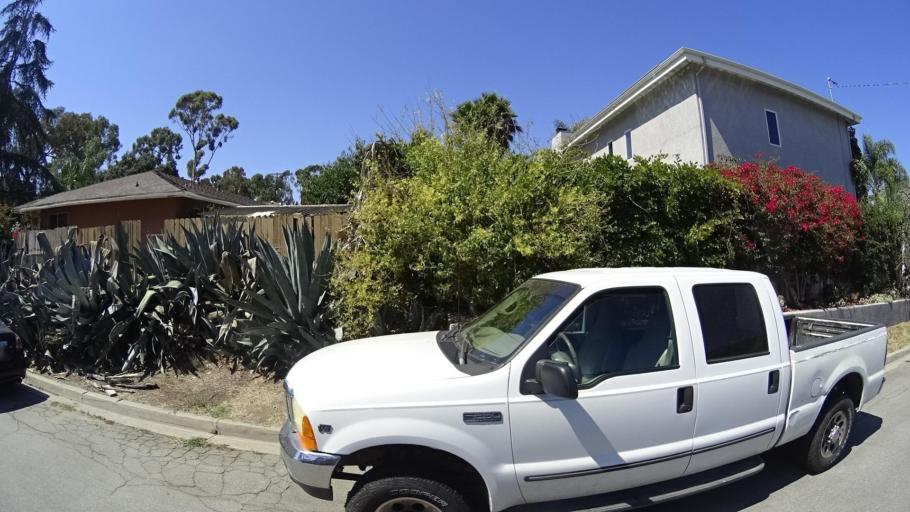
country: US
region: California
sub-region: San Diego County
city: Lake San Marcos
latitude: 33.1257
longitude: -117.2160
